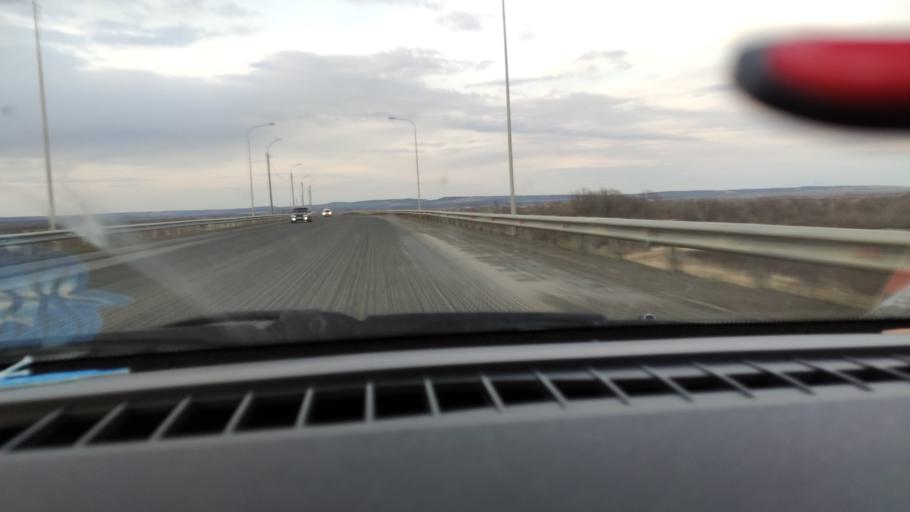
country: RU
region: Saratov
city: Yelshanka
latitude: 51.8031
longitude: 46.1911
